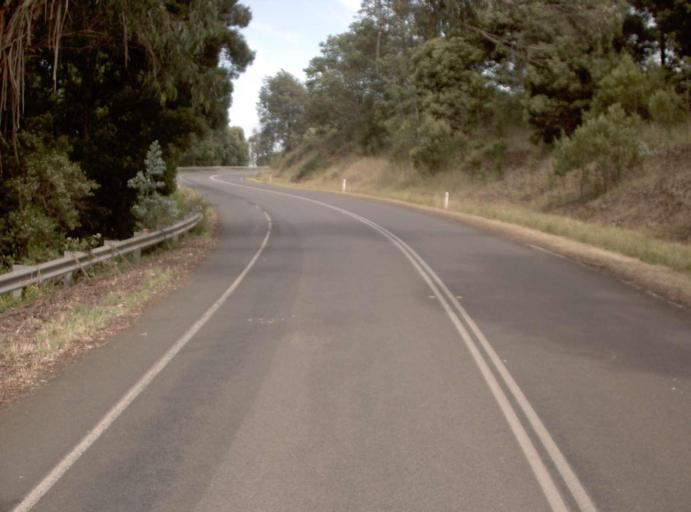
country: AU
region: Victoria
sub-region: Latrobe
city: Moe
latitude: -38.3312
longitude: 146.1799
